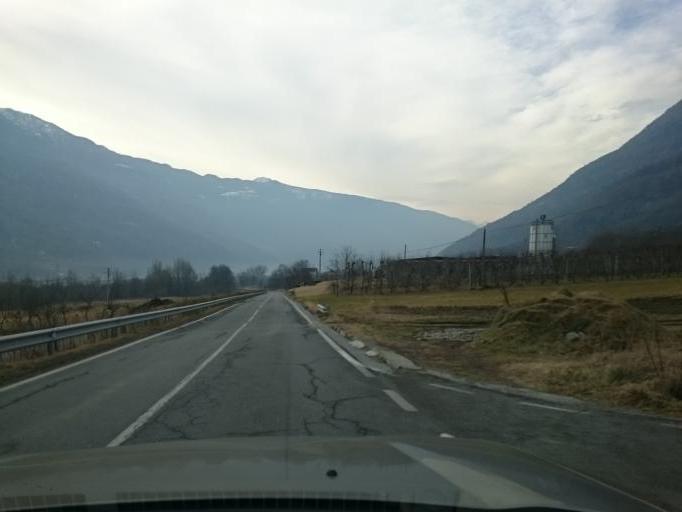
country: IT
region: Lombardy
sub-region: Provincia di Sondrio
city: Mazzo di Valtellina
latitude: 46.2688
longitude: 10.2540
